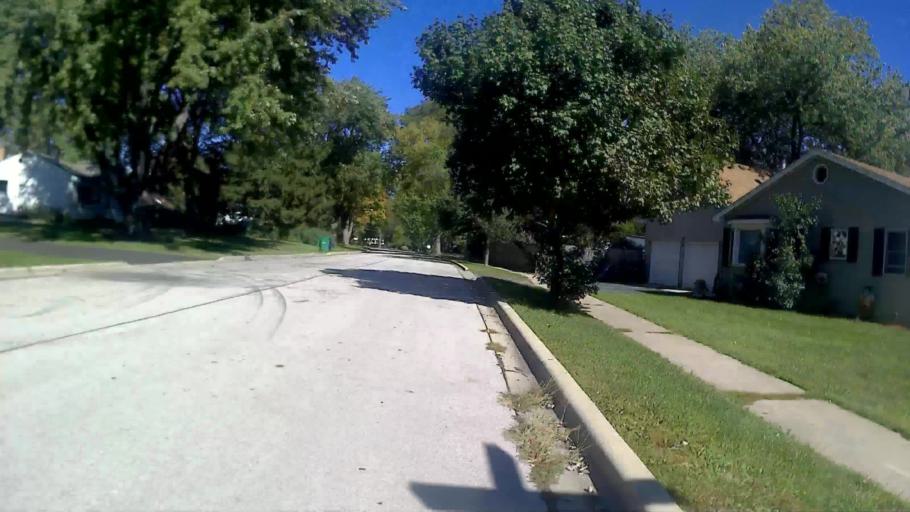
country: US
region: Illinois
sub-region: DuPage County
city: Lombard
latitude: 41.8984
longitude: -88.0251
